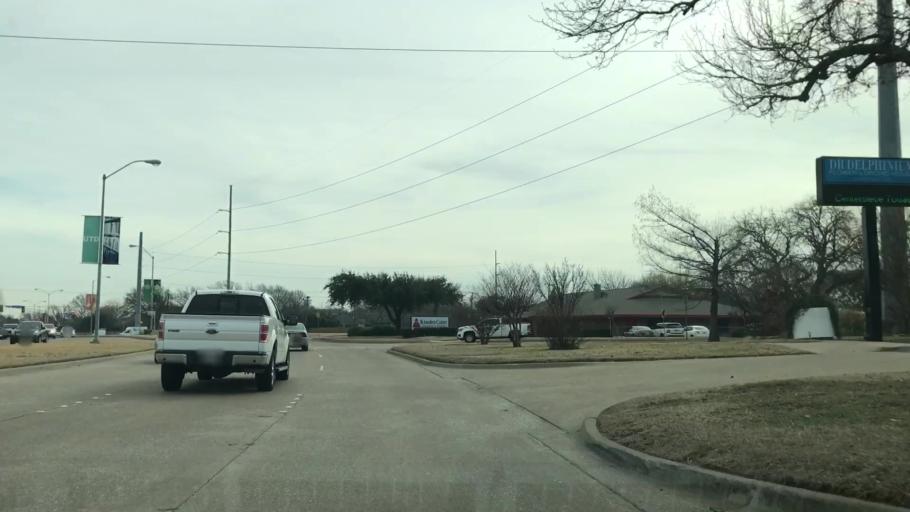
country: US
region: Texas
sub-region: Dallas County
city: Richardson
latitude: 32.9760
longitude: -96.7364
